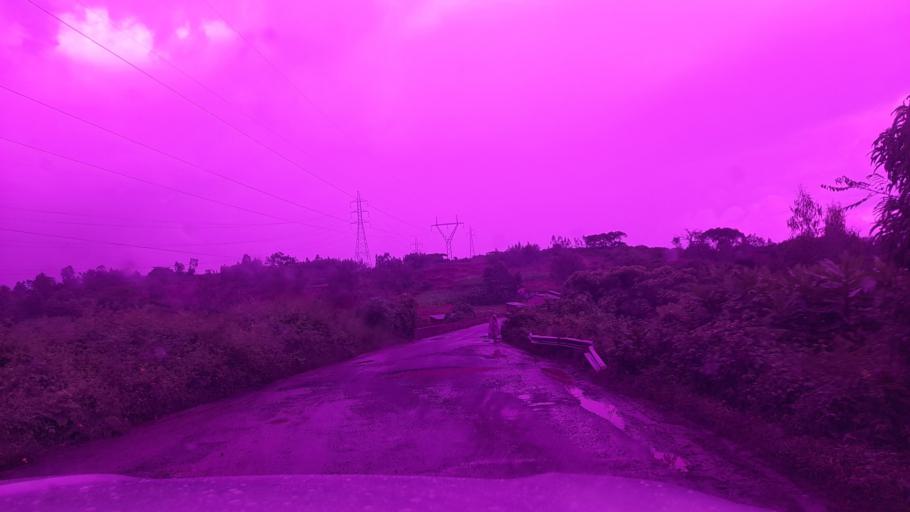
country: ET
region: Oromiya
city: Jima
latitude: 7.7142
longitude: 37.0861
